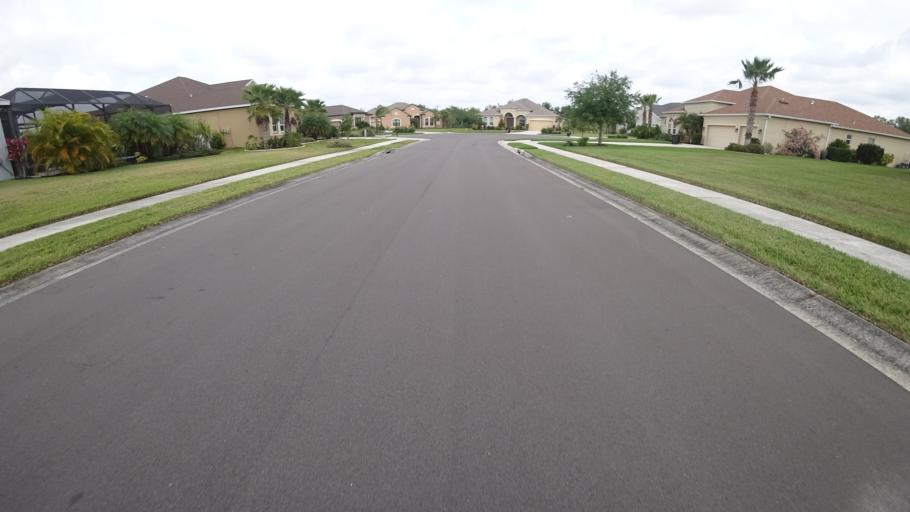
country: US
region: Florida
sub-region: Manatee County
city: Ellenton
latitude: 27.5342
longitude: -82.4099
